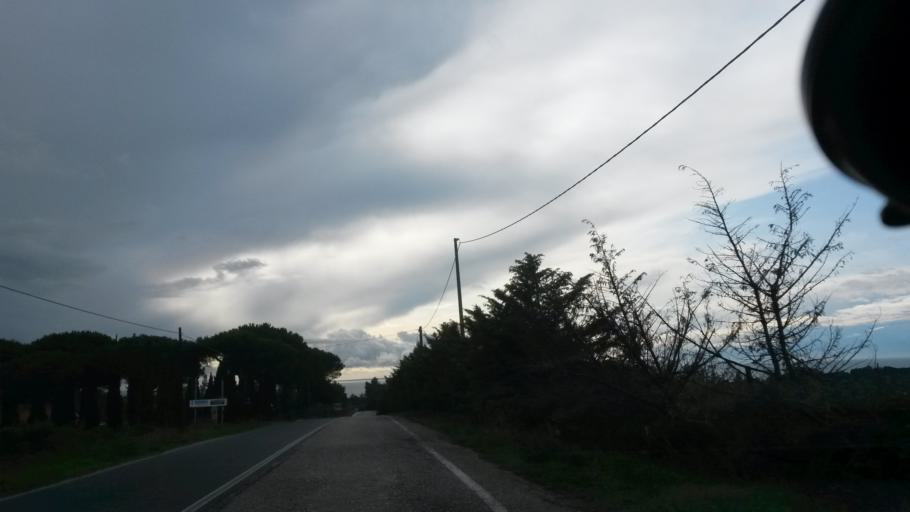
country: IT
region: Tuscany
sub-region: Provincia di Livorno
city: Rosignano Marittimo
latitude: 43.4173
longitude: 10.4540
